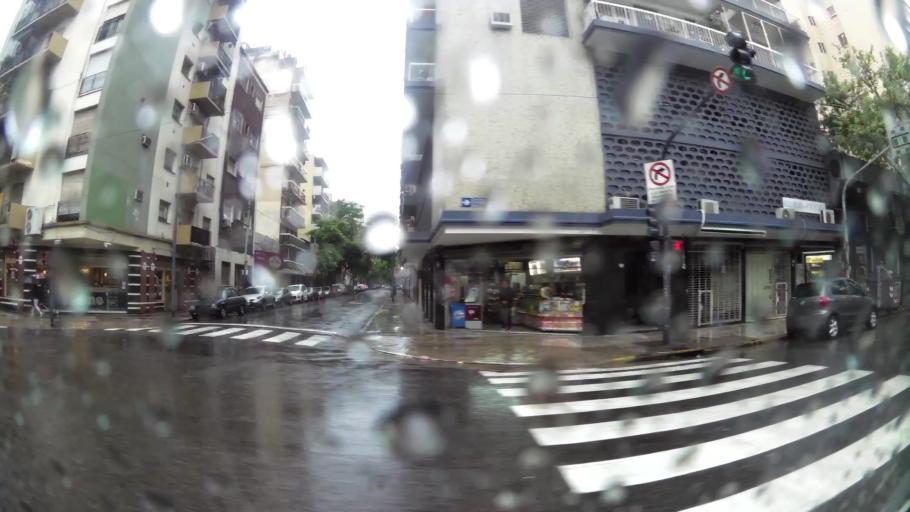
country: AR
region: Buenos Aires F.D.
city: Buenos Aires
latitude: -34.6156
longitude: -58.3918
